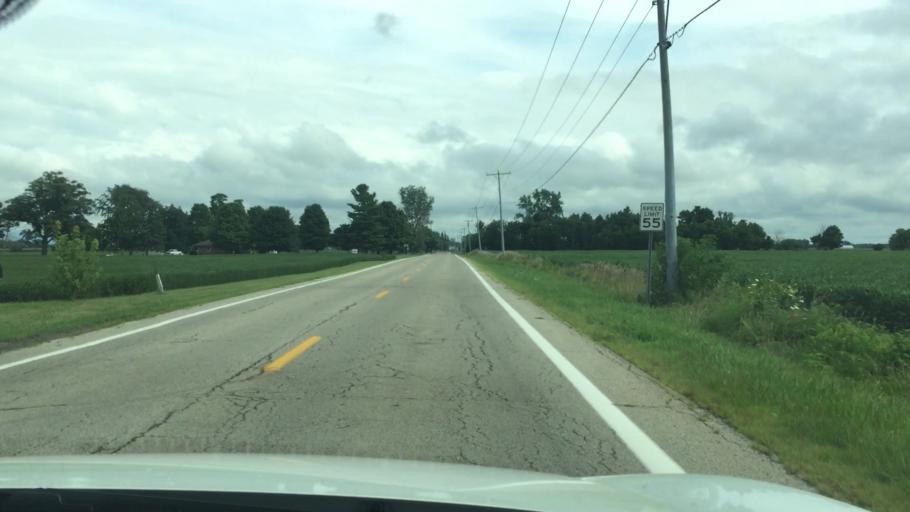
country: US
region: Ohio
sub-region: Champaign County
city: North Lewisburg
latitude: 40.2201
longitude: -83.5505
